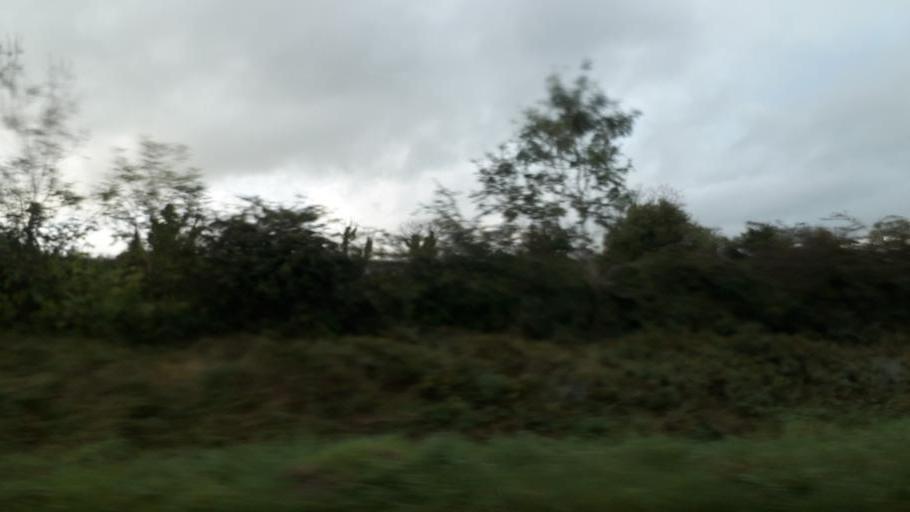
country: IE
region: Leinster
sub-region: An Longfort
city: Lanesborough
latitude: 53.7655
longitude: -8.0471
